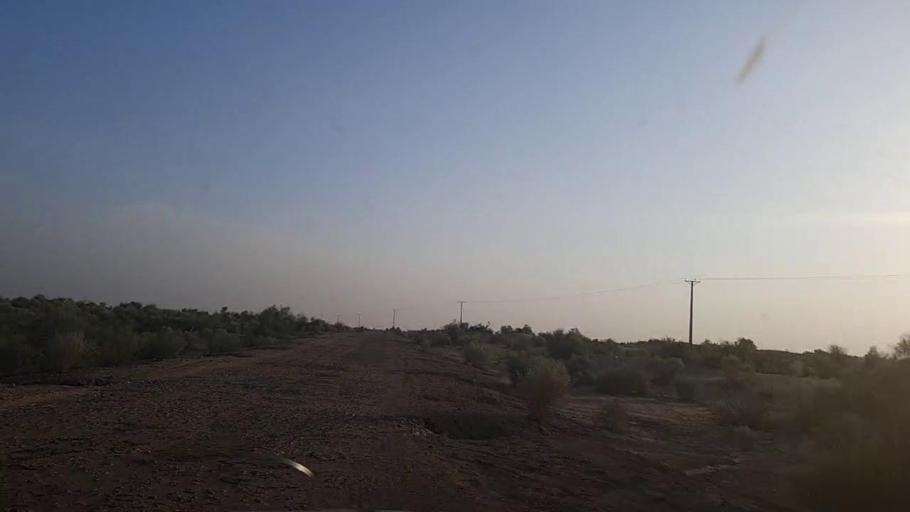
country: PK
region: Sindh
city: Khanpur
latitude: 27.6437
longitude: 69.4575
